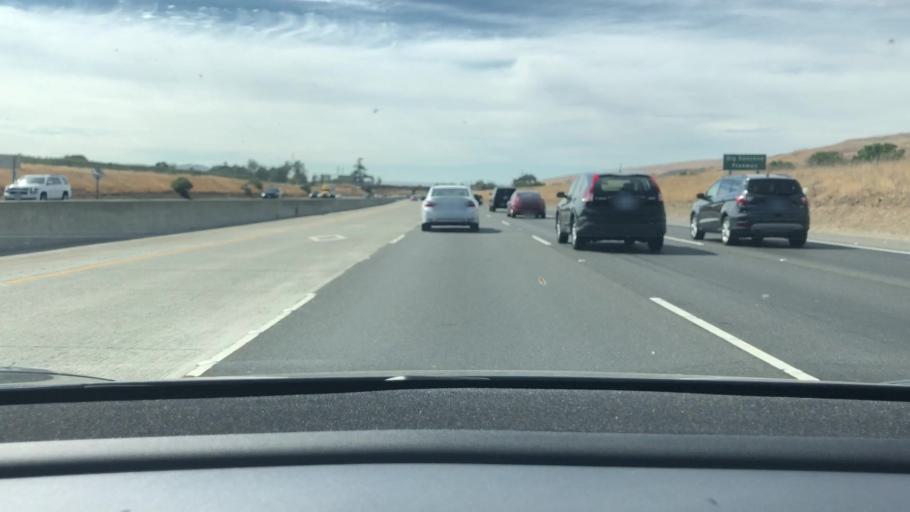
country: US
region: California
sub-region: Santa Clara County
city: Morgan Hill
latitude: 37.1592
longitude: -121.6585
